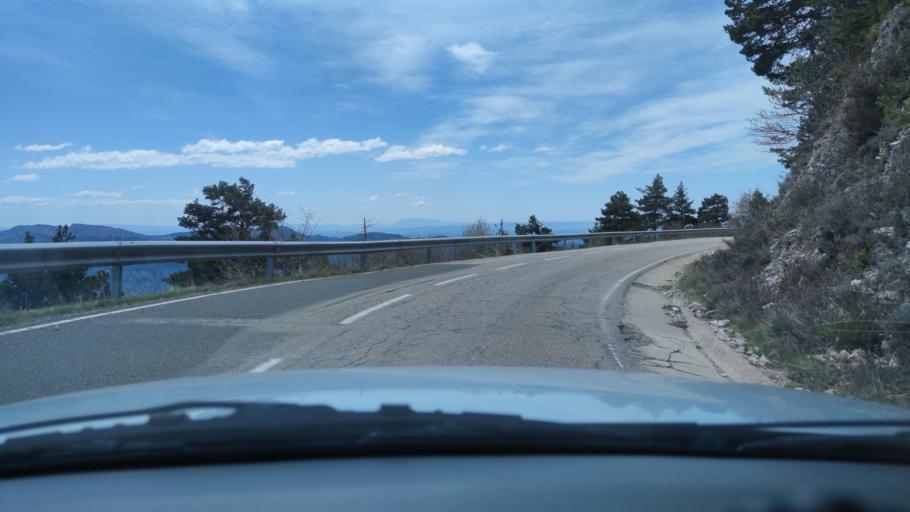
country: ES
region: Catalonia
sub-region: Provincia de Lleida
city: Gosol
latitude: 42.1598
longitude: 1.5750
